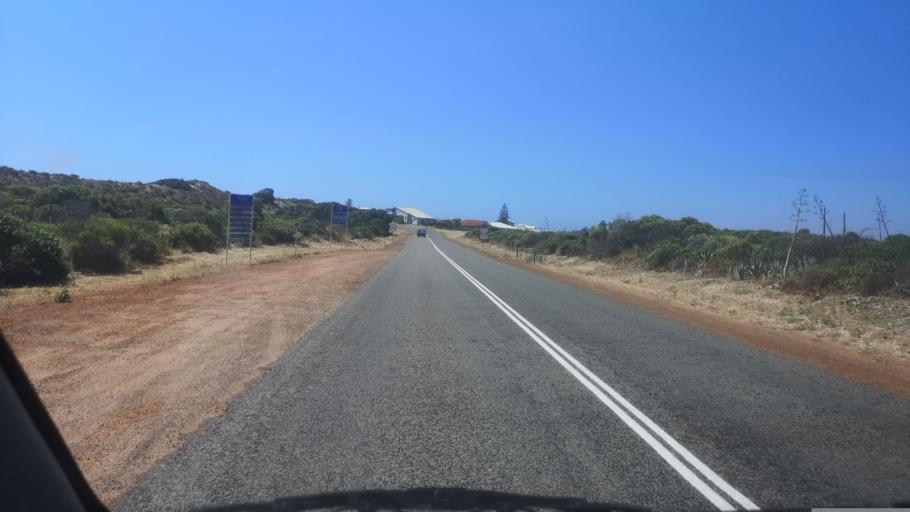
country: AU
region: Western Australia
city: Port Denison
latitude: -29.2831
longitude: 114.9228
